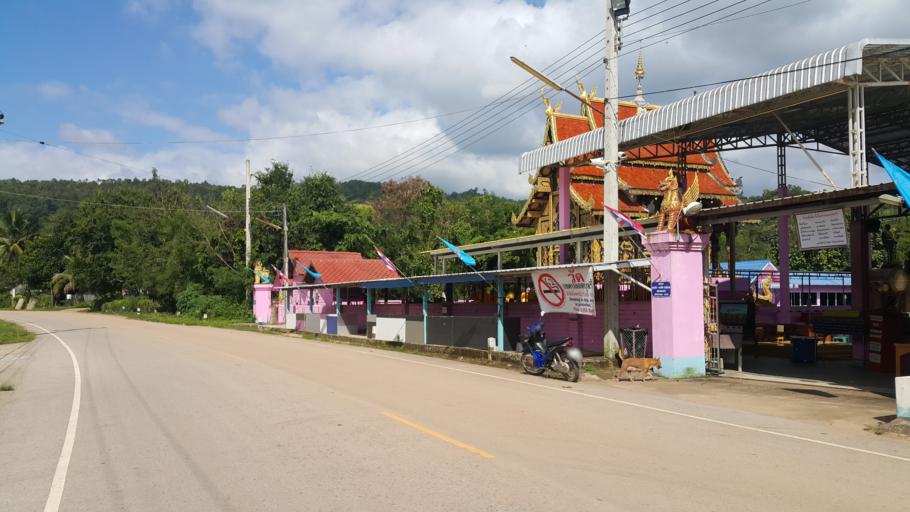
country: TH
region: Chiang Mai
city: Mae On
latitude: 18.7352
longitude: 99.3040
